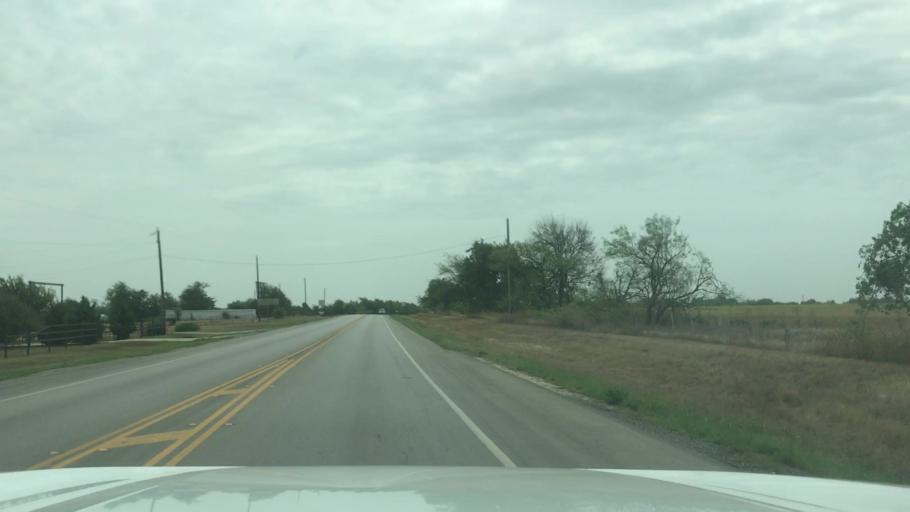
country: US
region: Texas
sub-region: Erath County
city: Dublin
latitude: 32.0927
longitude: -98.3667
